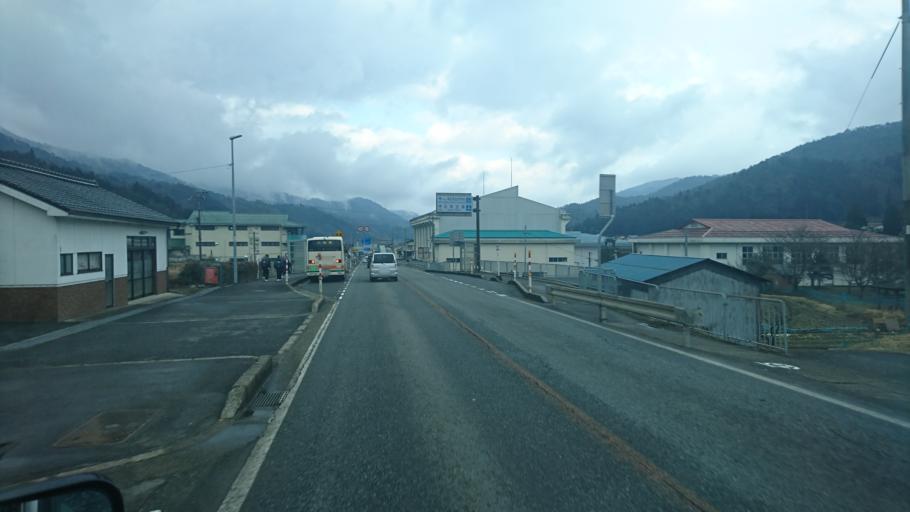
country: JP
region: Hyogo
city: Toyooka
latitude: 35.3752
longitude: 134.6424
